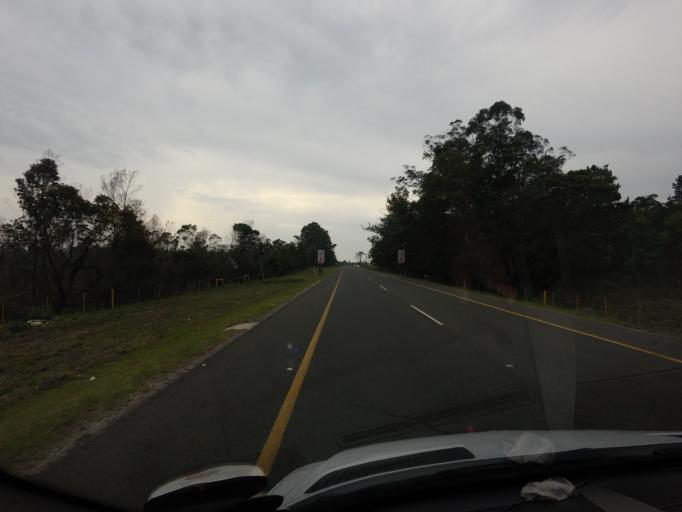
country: ZA
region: Western Cape
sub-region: Eden District Municipality
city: Plettenberg Bay
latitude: -34.0443
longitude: 23.3036
